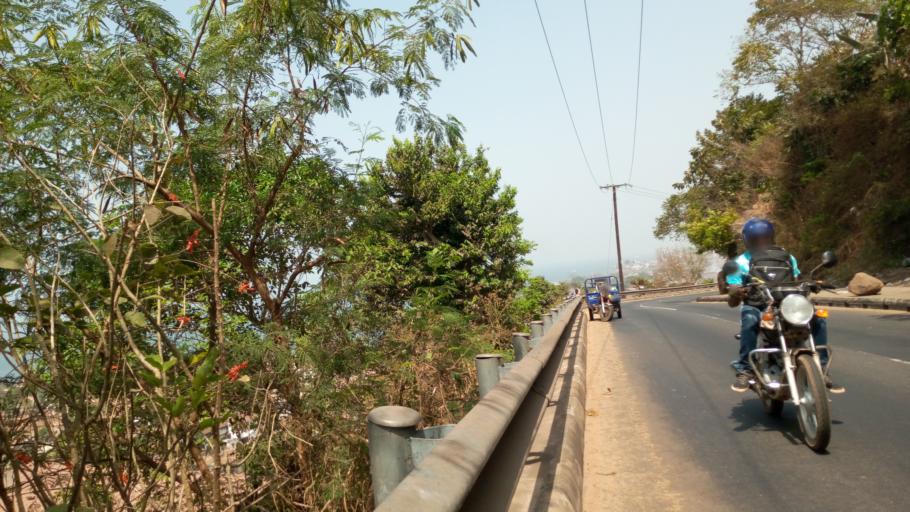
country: SL
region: Western Area
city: Freetown
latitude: 8.4835
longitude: -13.2662
